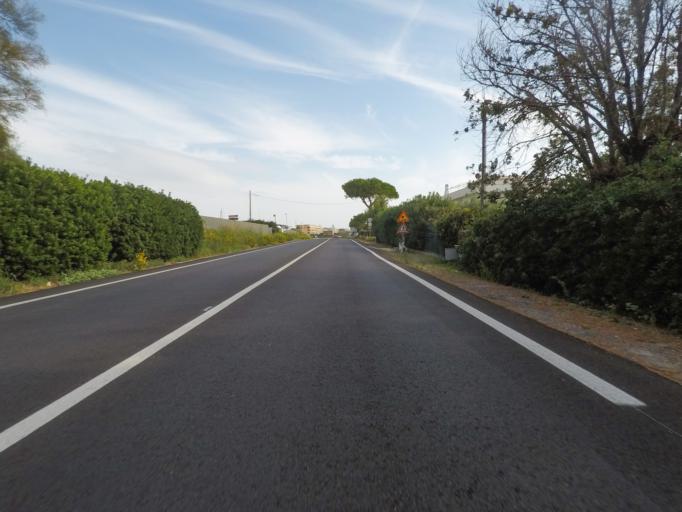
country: IT
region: Latium
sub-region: Citta metropolitana di Roma Capitale
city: Santa Marinella
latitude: 42.0462
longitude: 11.8240
